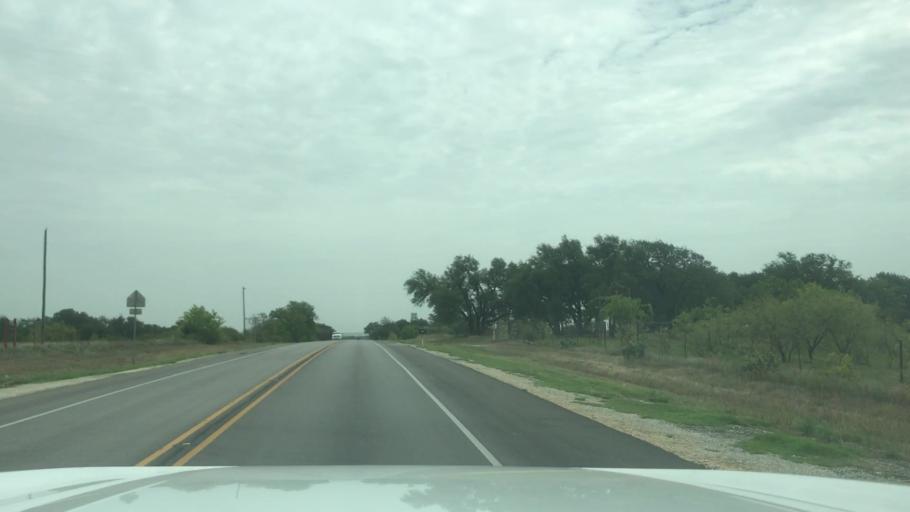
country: US
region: Texas
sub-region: Erath County
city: Dublin
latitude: 32.0858
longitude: -98.3165
